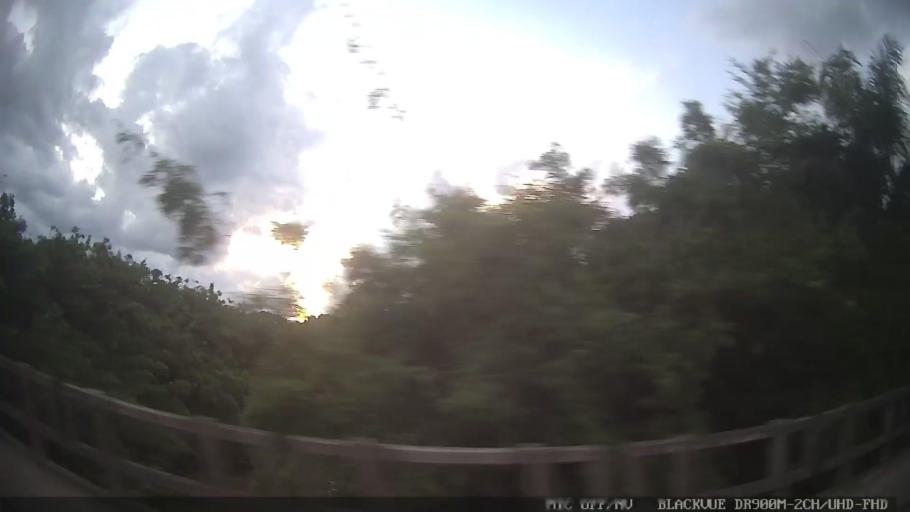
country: BR
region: Sao Paulo
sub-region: Itatiba
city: Itatiba
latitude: -22.9887
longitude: -46.7855
